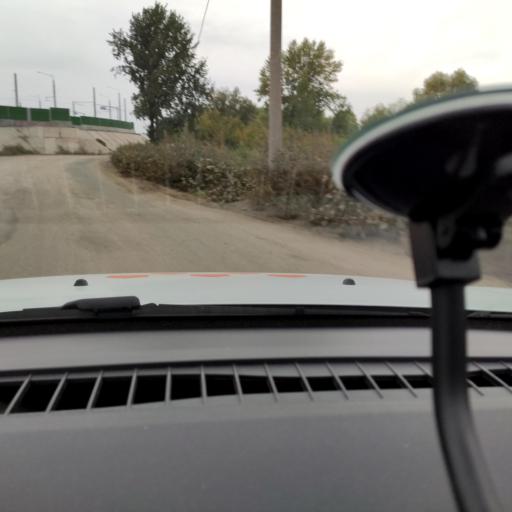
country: RU
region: Samara
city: Samara
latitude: 53.1651
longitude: 50.0925
